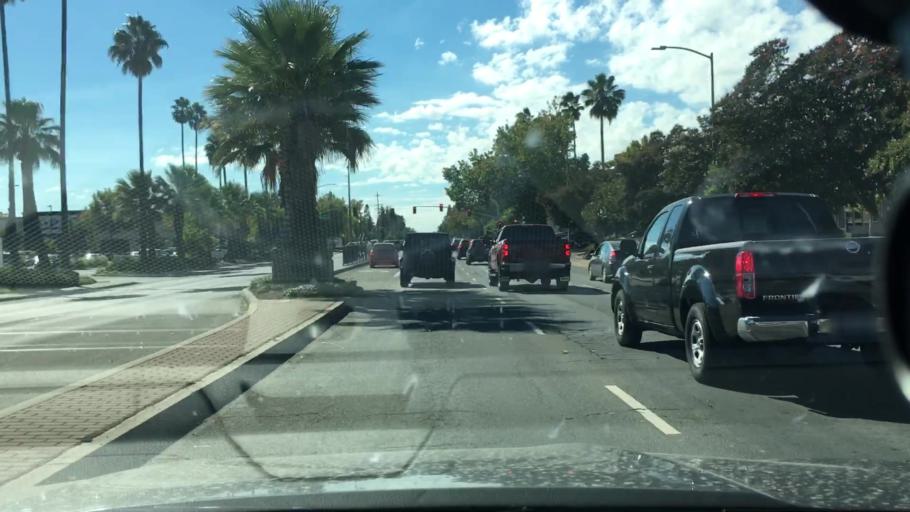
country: US
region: California
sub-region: Sacramento County
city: Arden-Arcade
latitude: 38.6080
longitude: -121.3831
